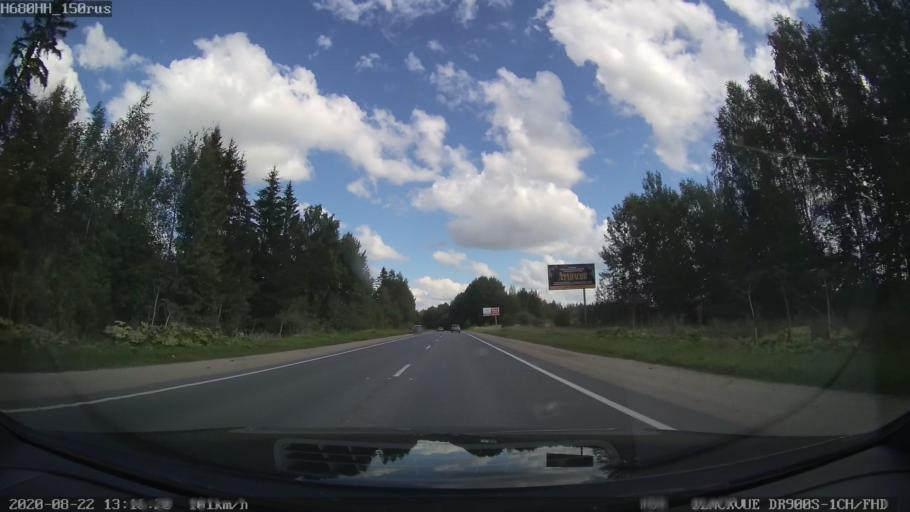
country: RU
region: Tverskaya
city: Bezhetsk
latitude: 57.7637
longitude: 36.6525
